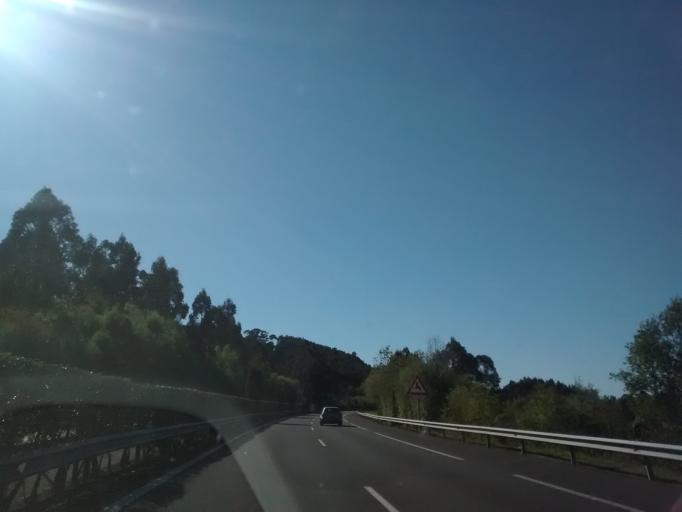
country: ES
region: Cantabria
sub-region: Provincia de Cantabria
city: Liendo
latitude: 43.3812
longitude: -3.3783
